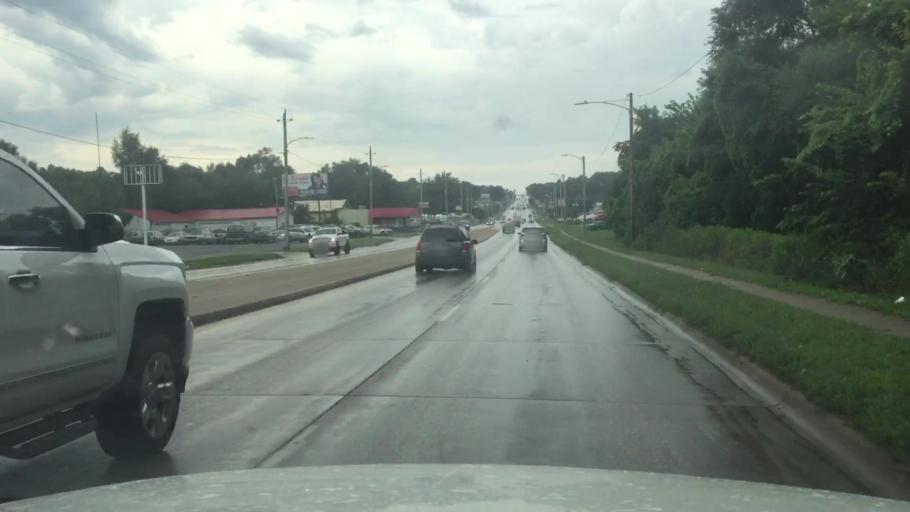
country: US
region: Iowa
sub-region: Polk County
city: Des Moines
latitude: 41.5738
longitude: -93.5970
